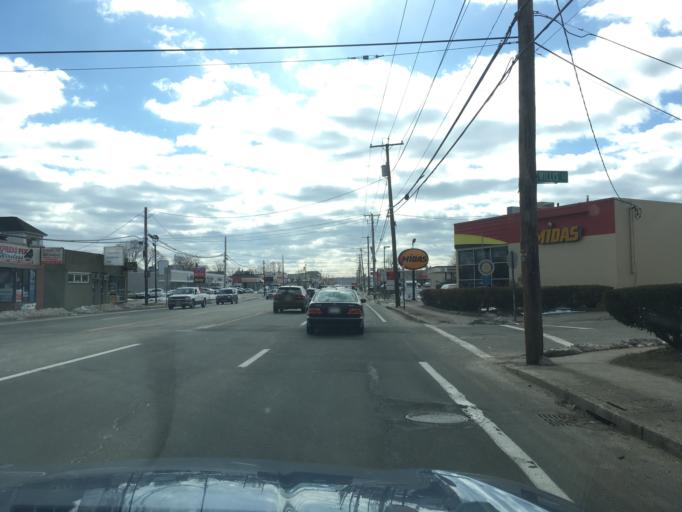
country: US
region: Rhode Island
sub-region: Providence County
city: Cranston
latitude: 41.7849
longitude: -71.4362
